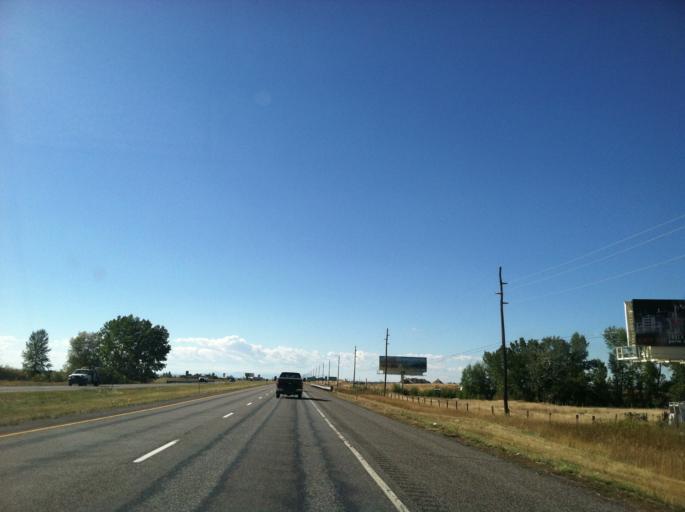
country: US
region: Montana
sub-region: Gallatin County
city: Belgrade
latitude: 45.7502
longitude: -111.1332
